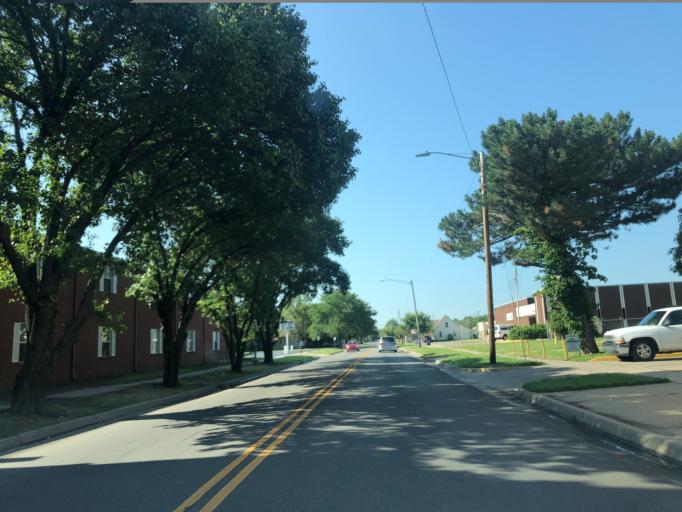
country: US
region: Kansas
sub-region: Sedgwick County
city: Wichita
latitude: 37.7262
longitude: -97.3448
